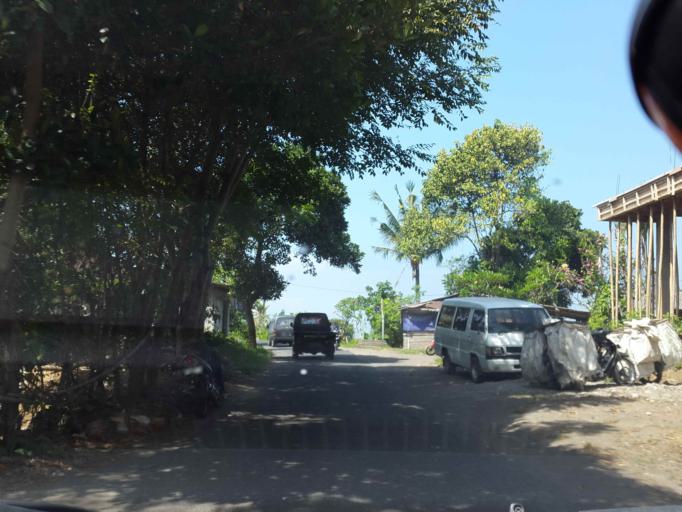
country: ID
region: Bali
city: Klungkung
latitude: -8.5518
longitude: 115.3669
